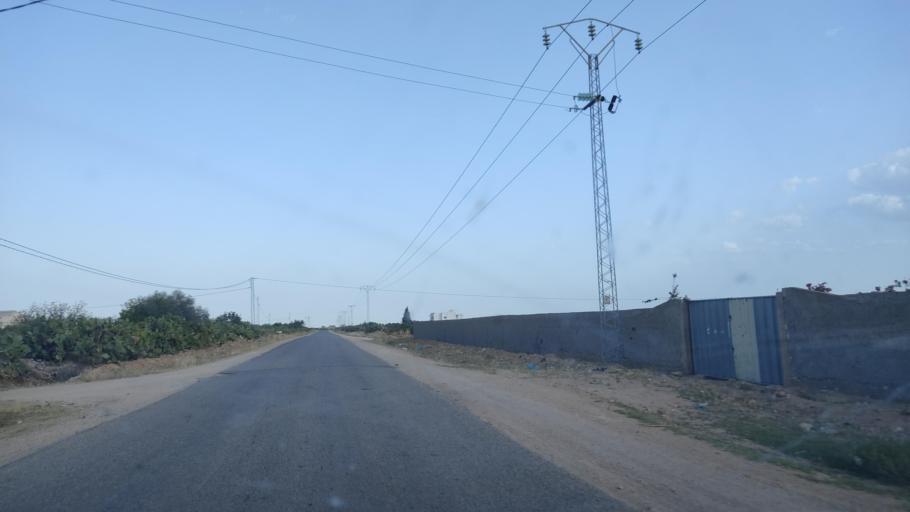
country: TN
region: Safaqis
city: Sfax
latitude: 34.8220
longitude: 10.6473
